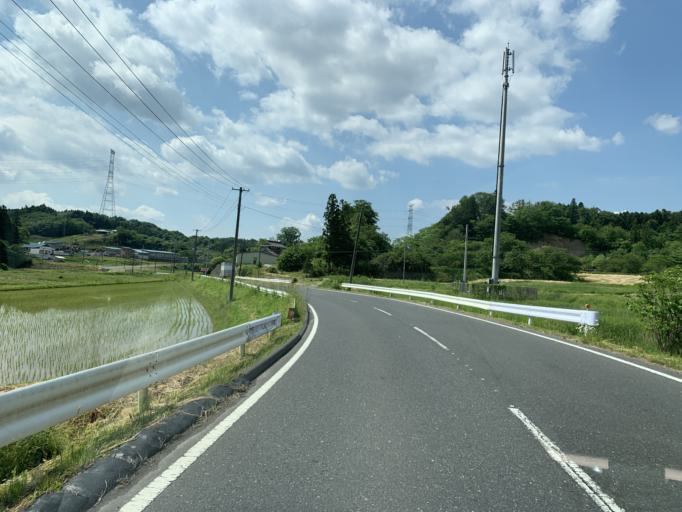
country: JP
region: Miyagi
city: Furukawa
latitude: 38.7839
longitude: 140.9580
